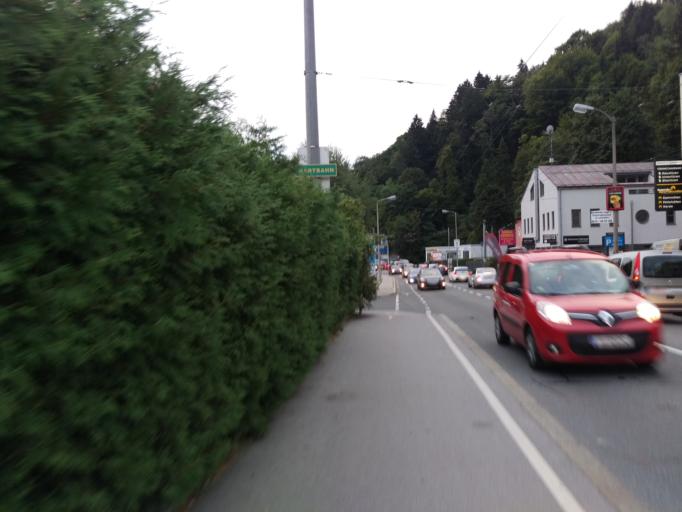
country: AT
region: Salzburg
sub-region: Salzburg Stadt
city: Salzburg
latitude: 47.8069
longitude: 13.0663
